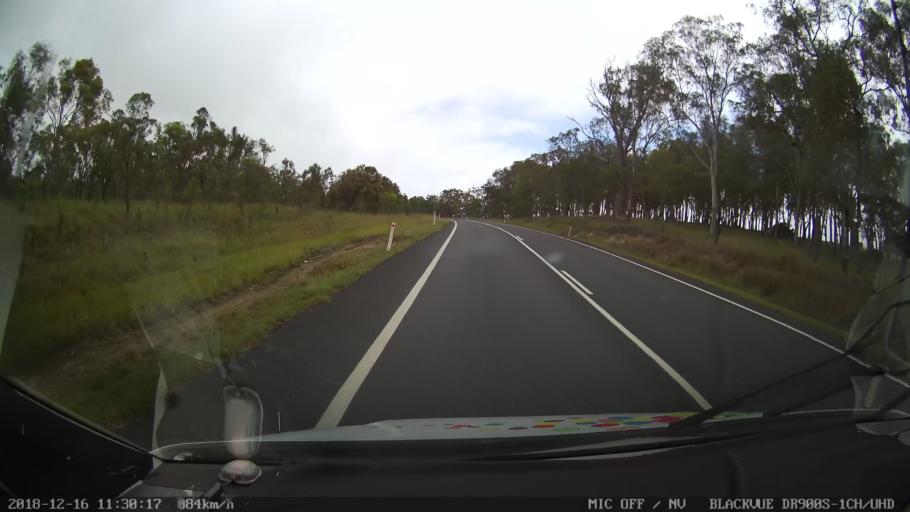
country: AU
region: New South Wales
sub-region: Tenterfield Municipality
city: Carrolls Creek
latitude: -29.0342
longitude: 152.1196
